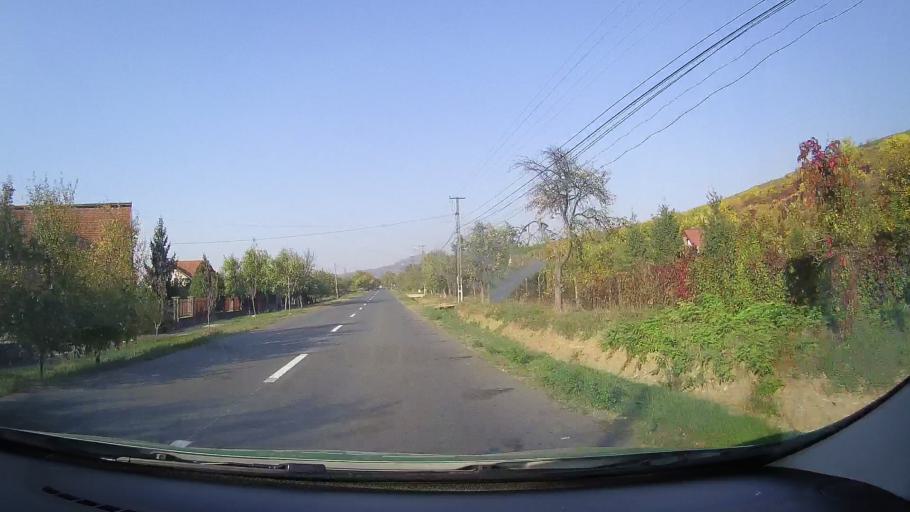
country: RO
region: Arad
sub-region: Comuna Paulis
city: Paulis
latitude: 46.1195
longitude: 21.5969
